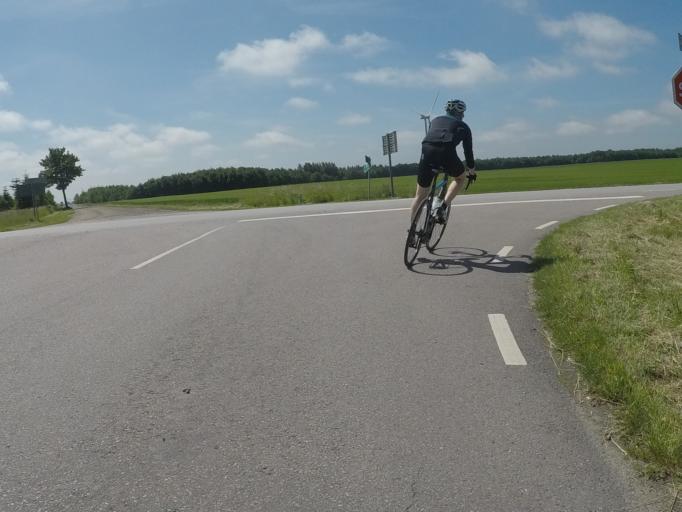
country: SE
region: Skane
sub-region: Malmo
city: Oxie
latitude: 55.5264
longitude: 13.1635
